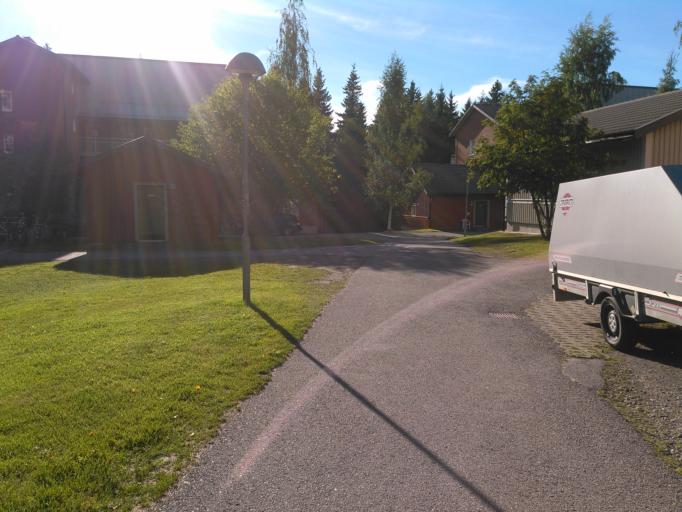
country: SE
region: Vaesterbotten
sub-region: Umea Kommun
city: Ersmark
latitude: 63.8266
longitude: 20.3253
